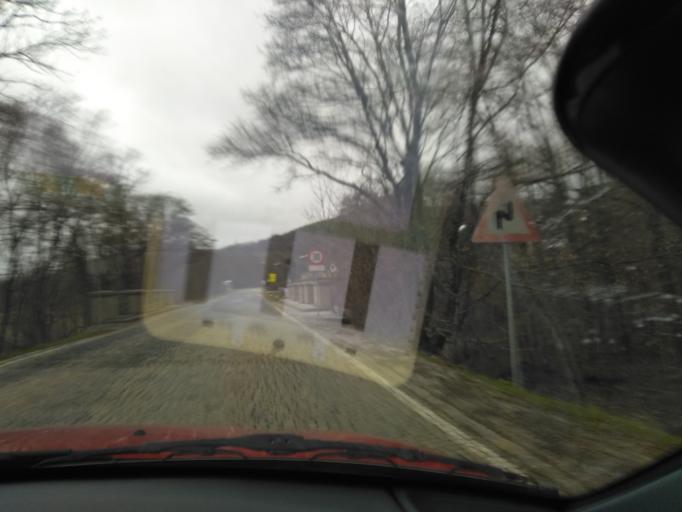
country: AT
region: Lower Austria
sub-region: Politischer Bezirk Wien-Umgebung
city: Klosterneuburg
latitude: 48.2507
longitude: 16.2829
